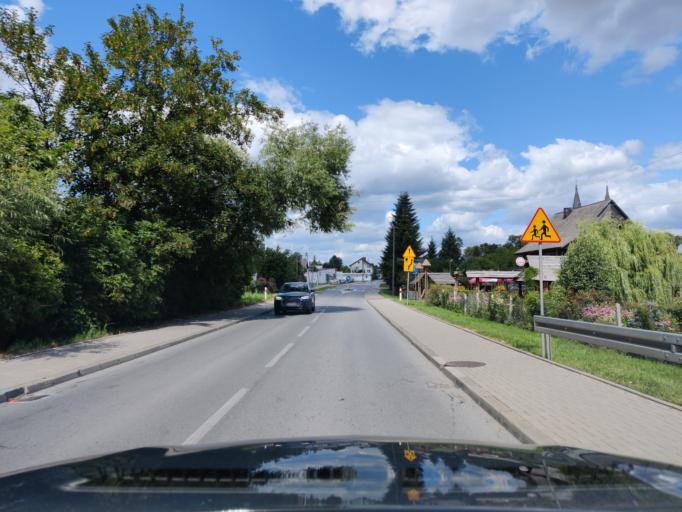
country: PL
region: Masovian Voivodeship
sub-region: Powiat wegrowski
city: Grebkow
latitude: 52.2678
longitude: 21.9096
